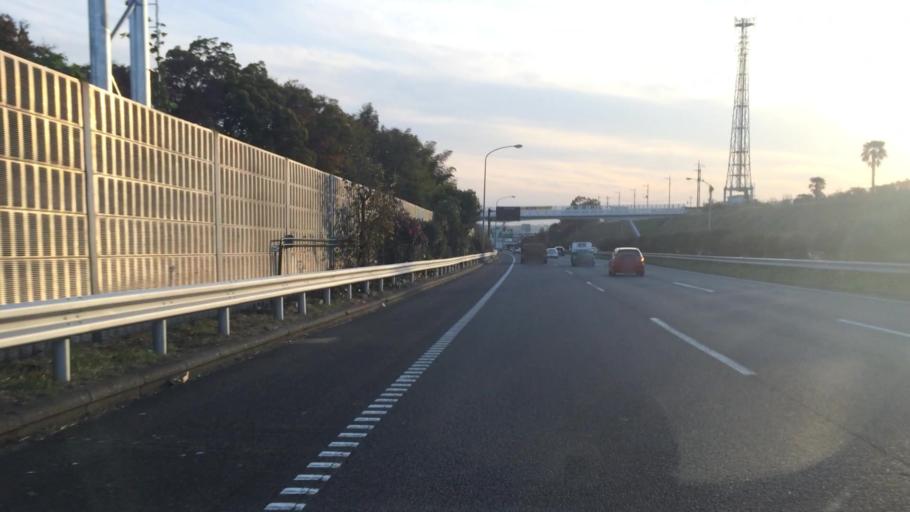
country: JP
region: Kanagawa
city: Yokohama
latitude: 35.5278
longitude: 139.5967
